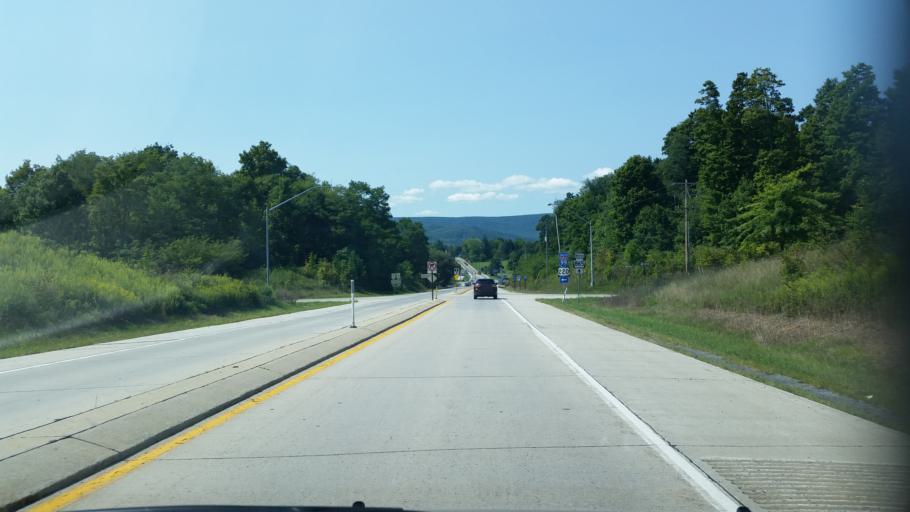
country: US
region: Pennsylvania
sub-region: Blair County
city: Bellwood
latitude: 40.5989
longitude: -78.3148
